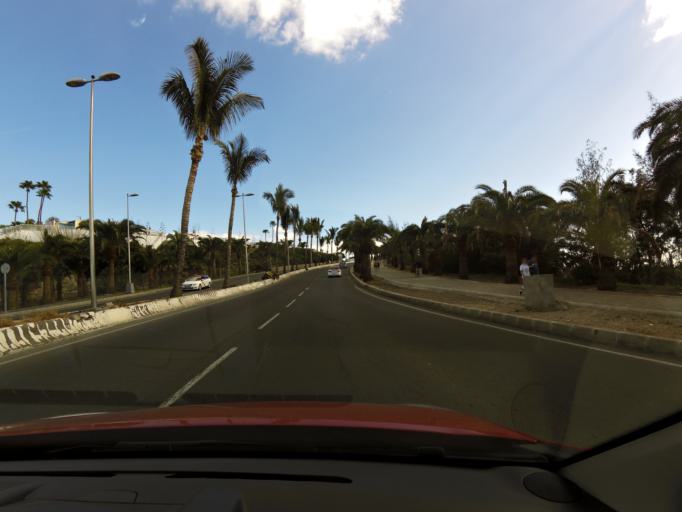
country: ES
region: Canary Islands
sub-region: Provincia de Las Palmas
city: Maspalomas
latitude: 27.7602
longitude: -15.5856
